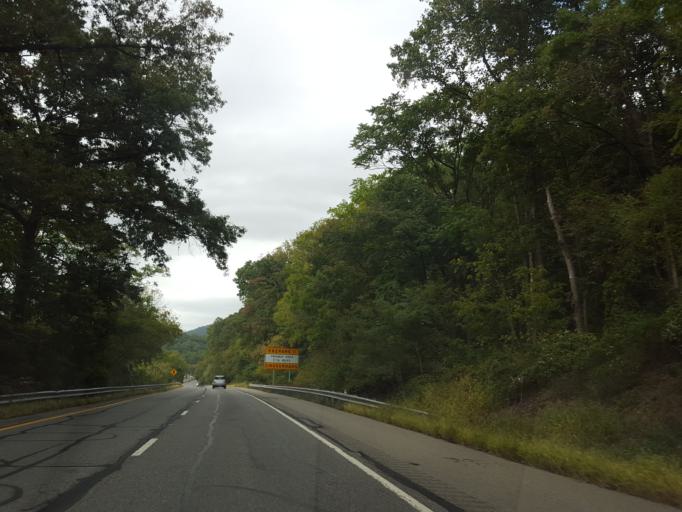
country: US
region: Maryland
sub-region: Frederick County
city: Brunswick
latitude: 39.3308
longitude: -77.6698
